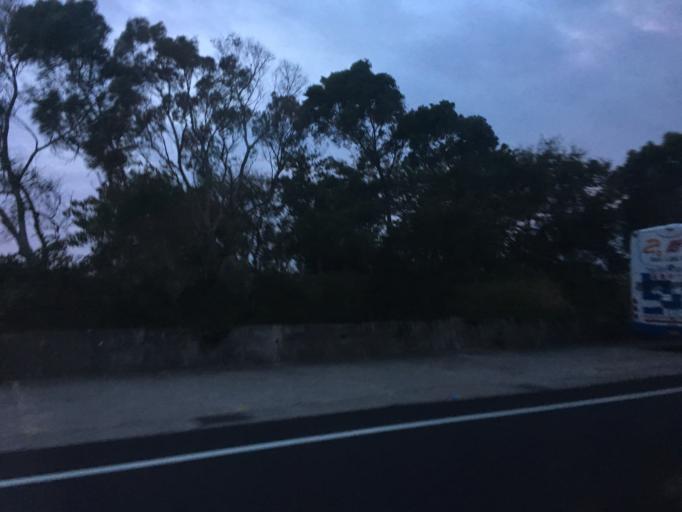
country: TW
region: Taiwan
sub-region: Hsinchu
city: Hsinchu
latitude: 24.7858
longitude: 120.9560
